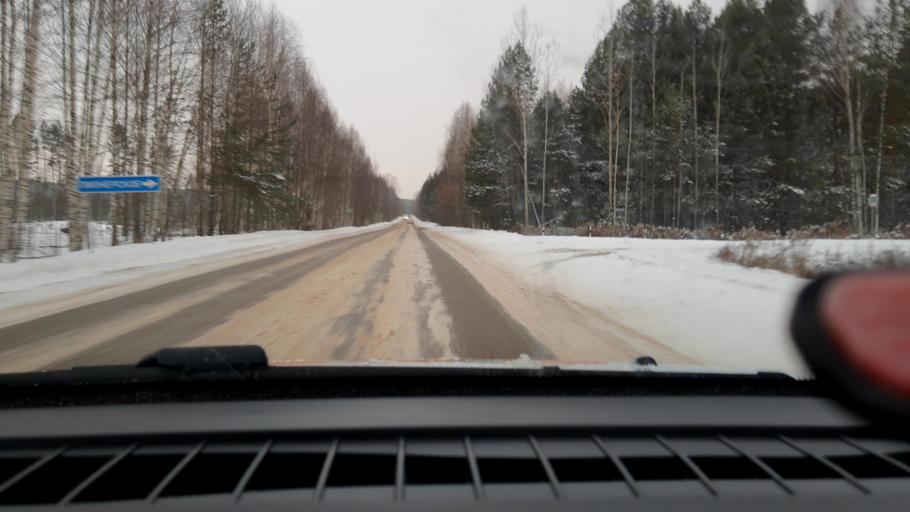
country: RU
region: Nizjnij Novgorod
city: Pamyat' Parizhskoy Kommuny
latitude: 56.2732
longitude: 44.4073
